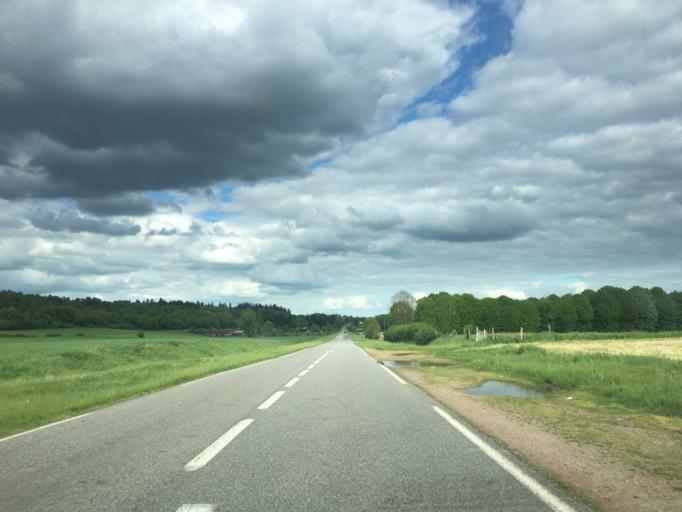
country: FR
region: Haute-Normandie
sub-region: Departement de l'Eure
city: Nonancourt
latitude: 48.7721
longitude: 1.1685
